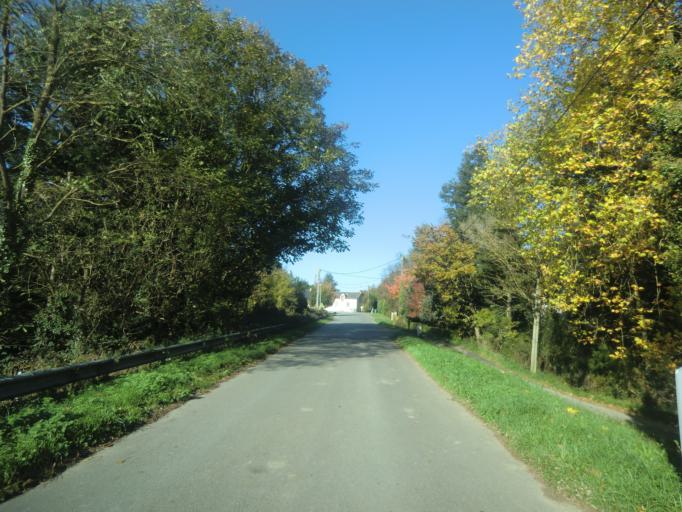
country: FR
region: Pays de la Loire
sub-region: Departement de la Loire-Atlantique
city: Blain
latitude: 47.4702
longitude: -1.7209
